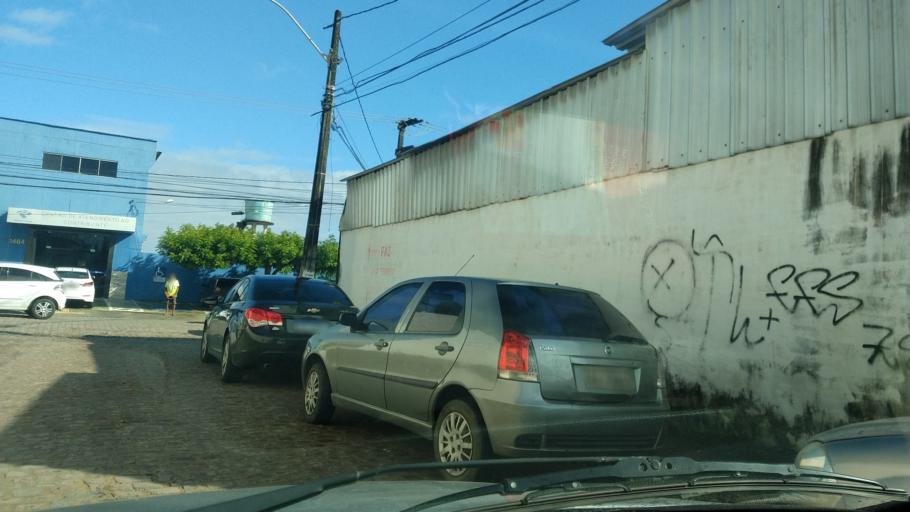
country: BR
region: Rio Grande do Norte
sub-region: Parnamirim
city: Parnamirim
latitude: -5.9163
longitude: -35.2635
